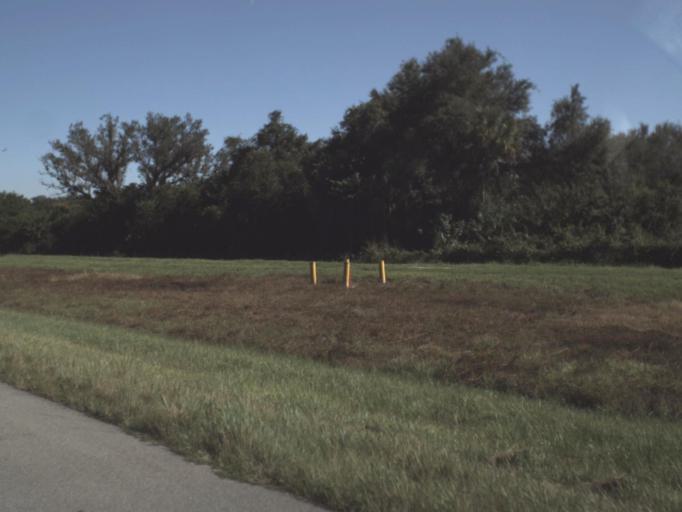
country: US
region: Florida
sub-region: Hendry County
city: Port LaBelle
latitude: 26.7618
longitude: -81.4202
